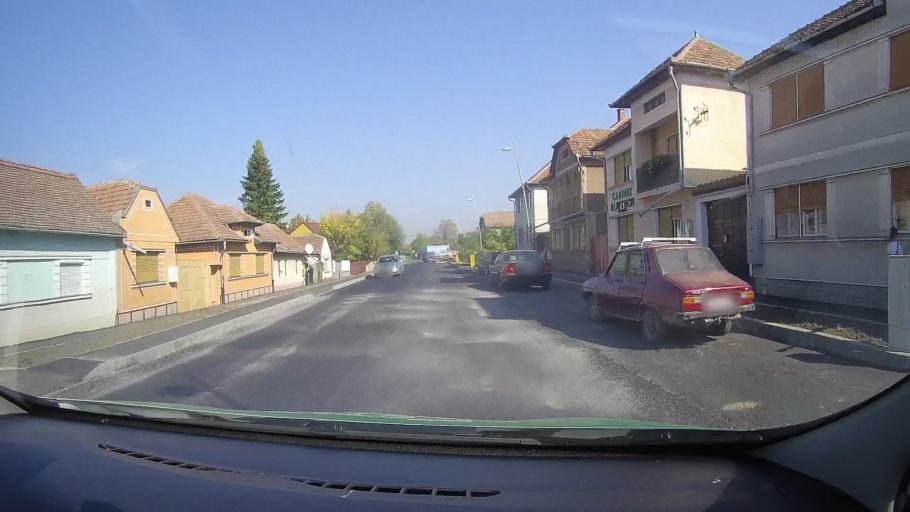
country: RO
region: Bihor
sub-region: Municipiul Salonta
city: Salonta
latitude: 46.7957
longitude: 21.6653
